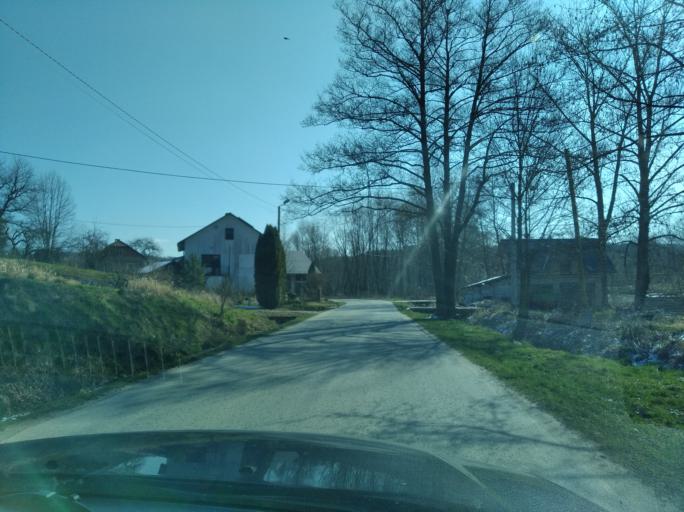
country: PL
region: Subcarpathian Voivodeship
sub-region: Powiat strzyzowski
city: Jawornik
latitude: 49.8454
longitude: 21.8855
